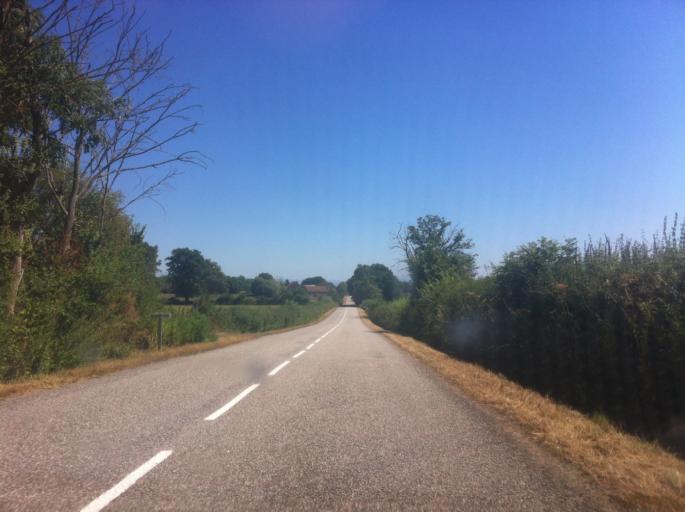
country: FR
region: Auvergne
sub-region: Departement de l'Allier
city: Montmarault
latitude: 46.2934
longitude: 3.0308
